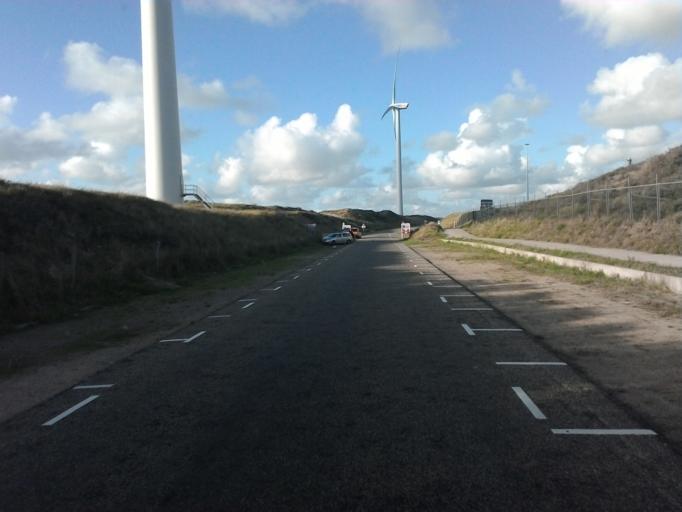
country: NL
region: North Holland
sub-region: Gemeente Velsen
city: Velsen-Zuid
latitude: 52.4722
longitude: 4.5746
